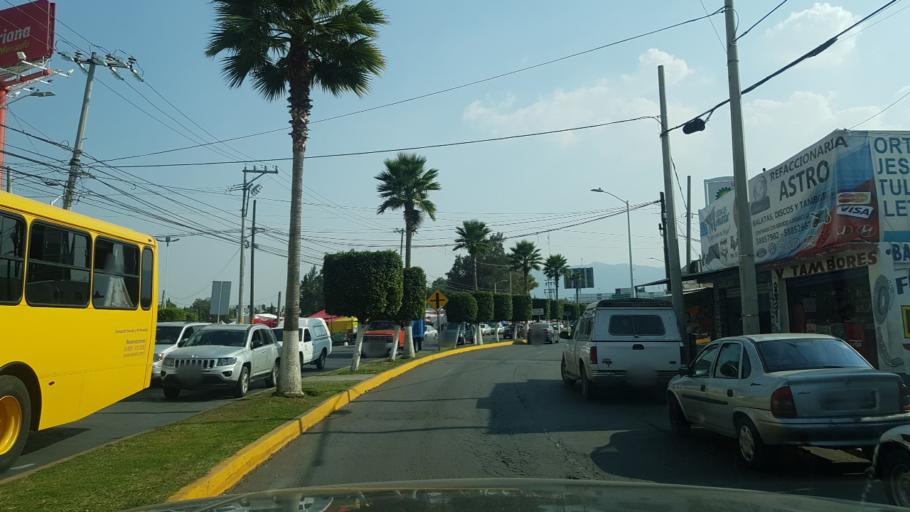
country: MX
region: Mexico
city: Santiago Teyahualco
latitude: 19.6546
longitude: -99.1205
